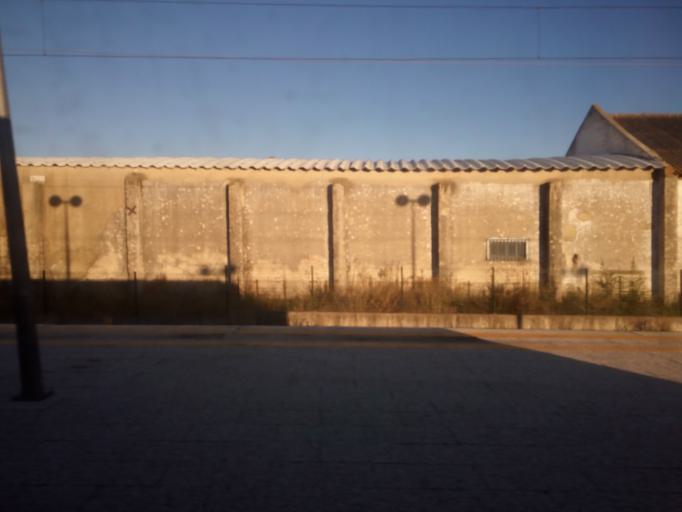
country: PT
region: Setubal
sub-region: Grandola
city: Grandola
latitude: 38.1831
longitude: -8.5547
